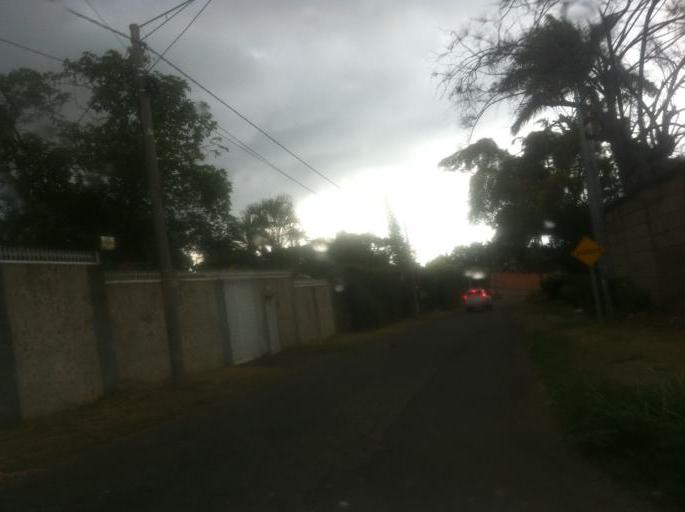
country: NI
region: Managua
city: Managua
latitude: 12.0968
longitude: -86.2356
